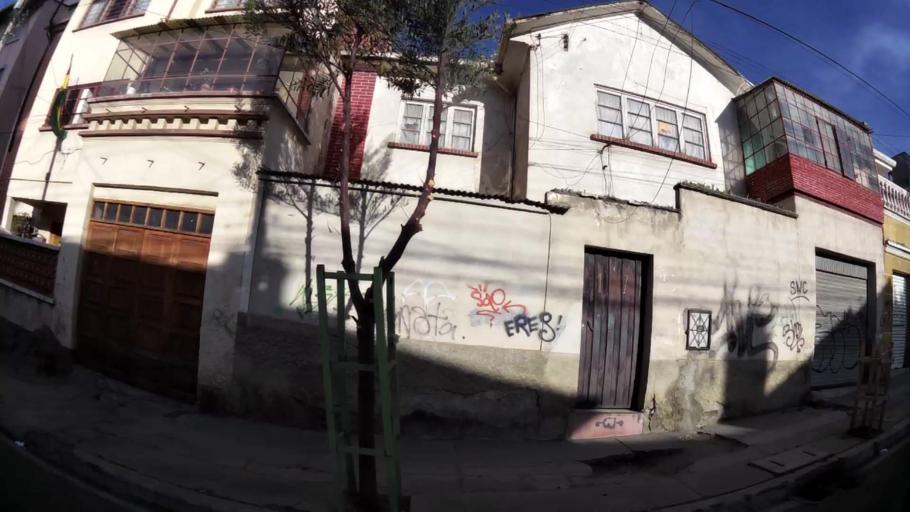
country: BO
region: La Paz
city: La Paz
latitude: -16.4905
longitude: -68.1223
